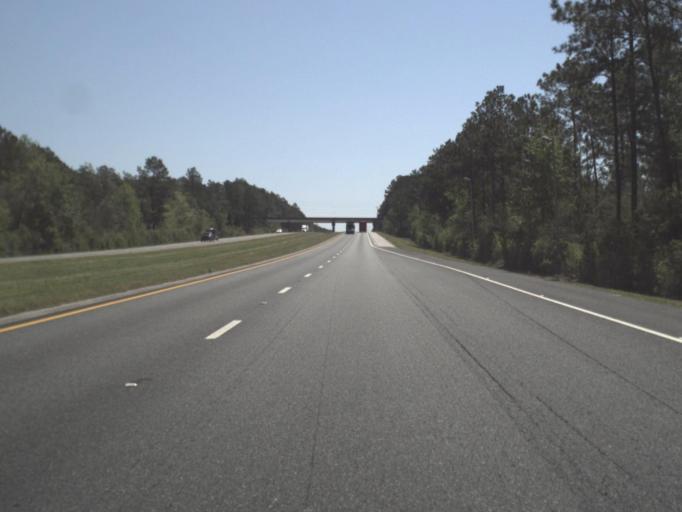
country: US
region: Florida
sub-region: Escambia County
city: Cantonment
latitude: 30.5670
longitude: -87.3913
